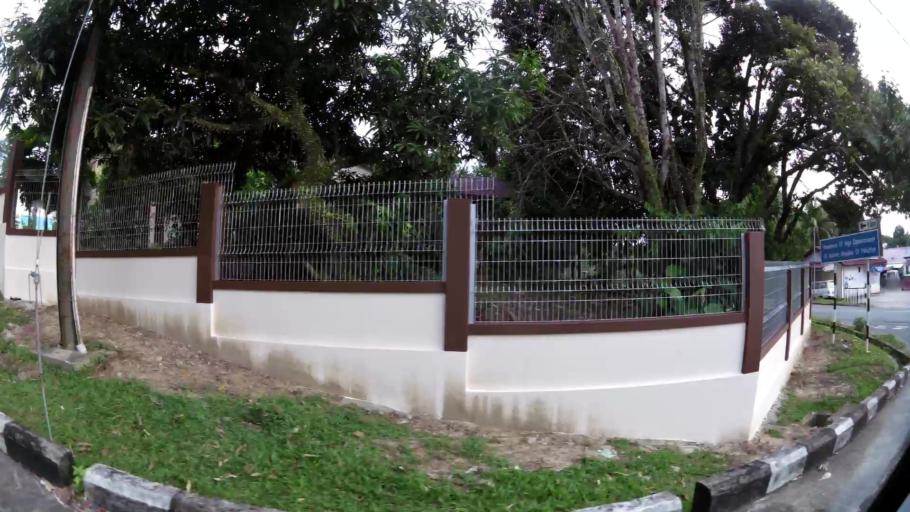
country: BN
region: Brunei and Muara
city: Bandar Seri Begawan
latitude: 4.9178
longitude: 114.8947
